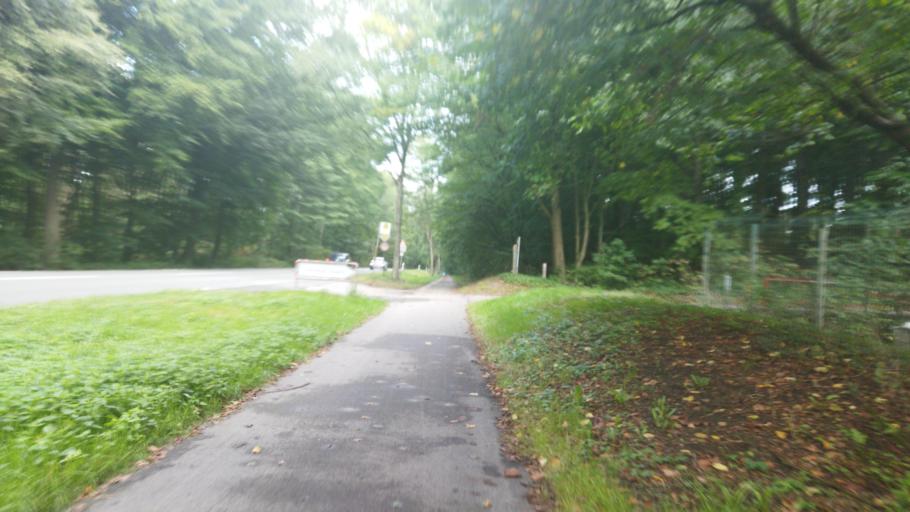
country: DE
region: North Rhine-Westphalia
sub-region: Regierungsbezirk Munster
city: Haltern
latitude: 51.7148
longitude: 7.1909
